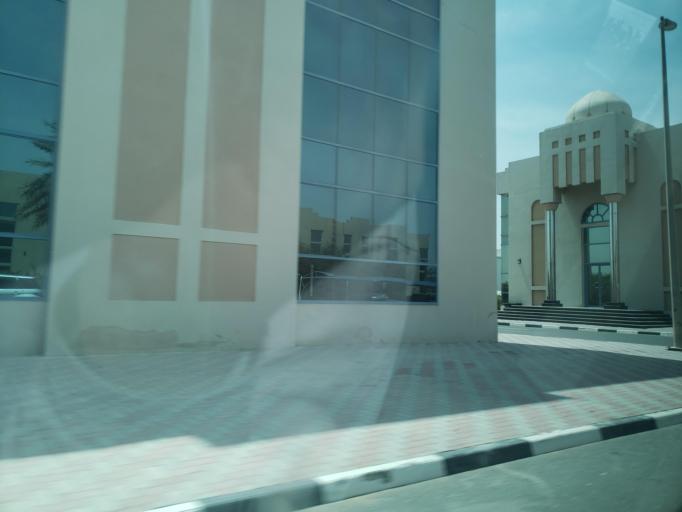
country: AE
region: Ash Shariqah
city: Sharjah
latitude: 25.3298
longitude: 55.4989
